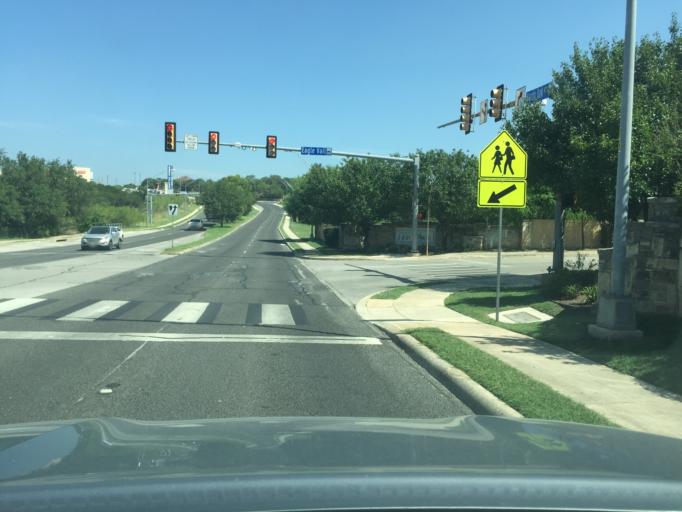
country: US
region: Texas
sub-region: Bexar County
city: Timberwood Park
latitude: 29.6579
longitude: -98.4966
